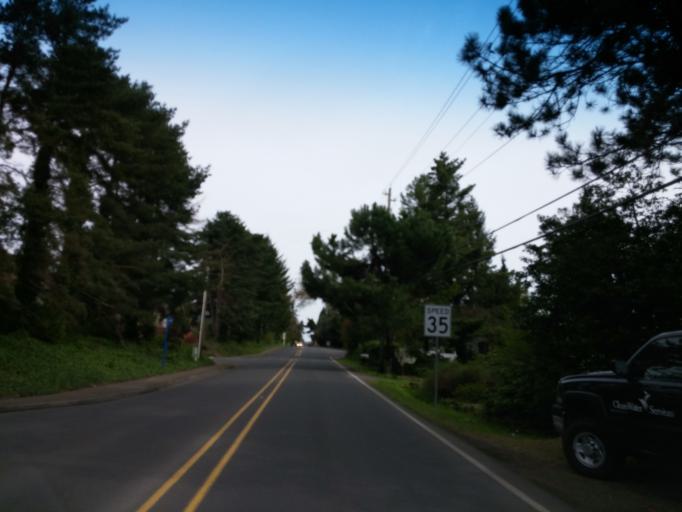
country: US
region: Oregon
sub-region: Washington County
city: Cedar Mill
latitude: 45.5273
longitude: -122.7997
